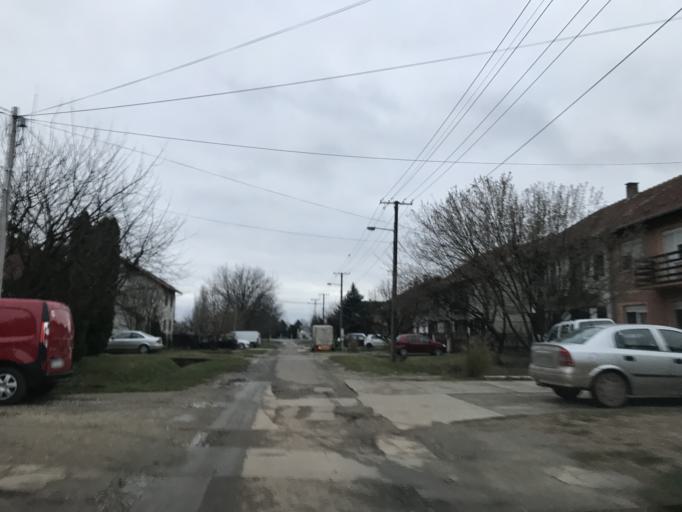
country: RS
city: Rumenka
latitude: 45.2970
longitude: 19.7344
